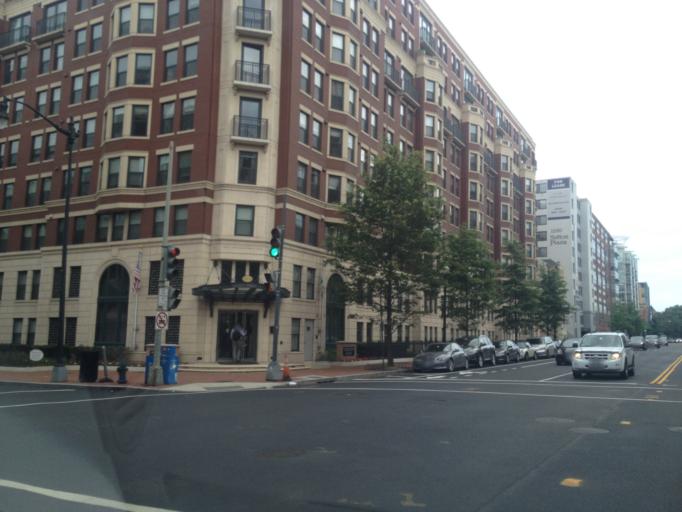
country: US
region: Washington, D.C.
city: Washington, D.C.
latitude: 38.9056
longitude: -77.0296
